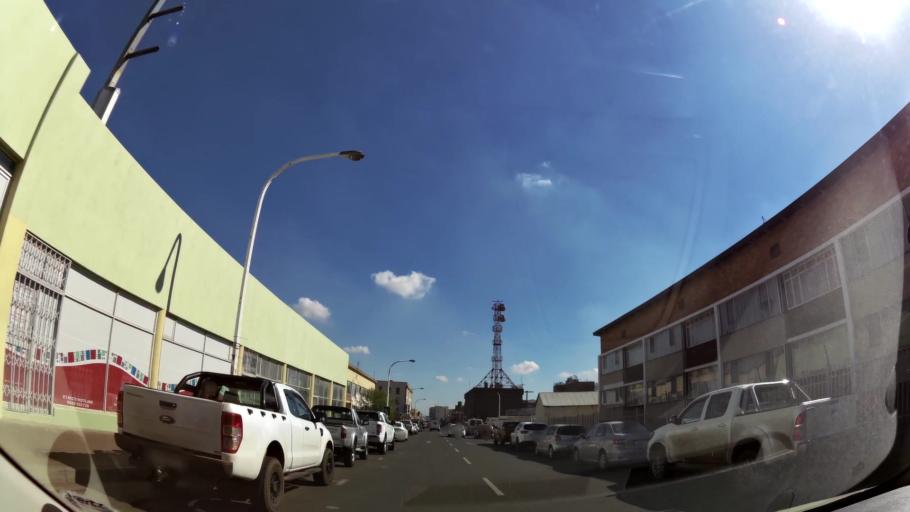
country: ZA
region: Mpumalanga
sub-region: Nkangala District Municipality
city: Witbank
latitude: -25.8760
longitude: 29.2162
